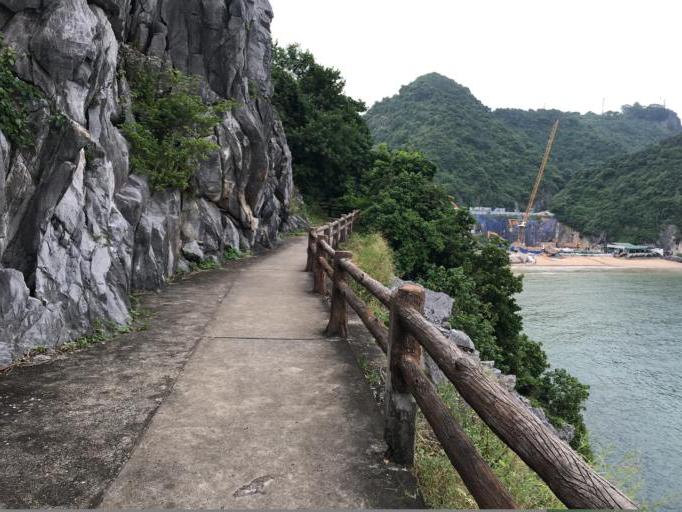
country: VN
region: Hai Phong
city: Cat Ba
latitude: 20.7156
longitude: 107.0524
